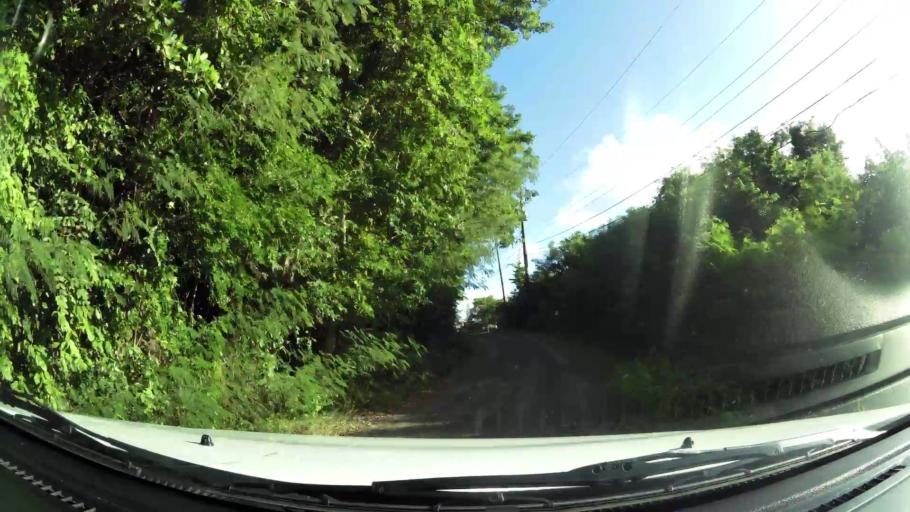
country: LC
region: Gros-Islet
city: Gros Islet
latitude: 14.1021
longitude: -60.9380
